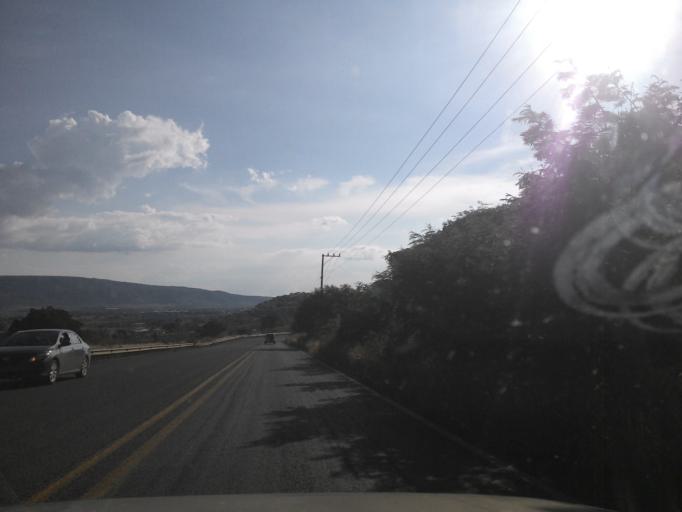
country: MX
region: Jalisco
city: Atotonilco el Alto
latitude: 20.5503
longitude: -102.5235
